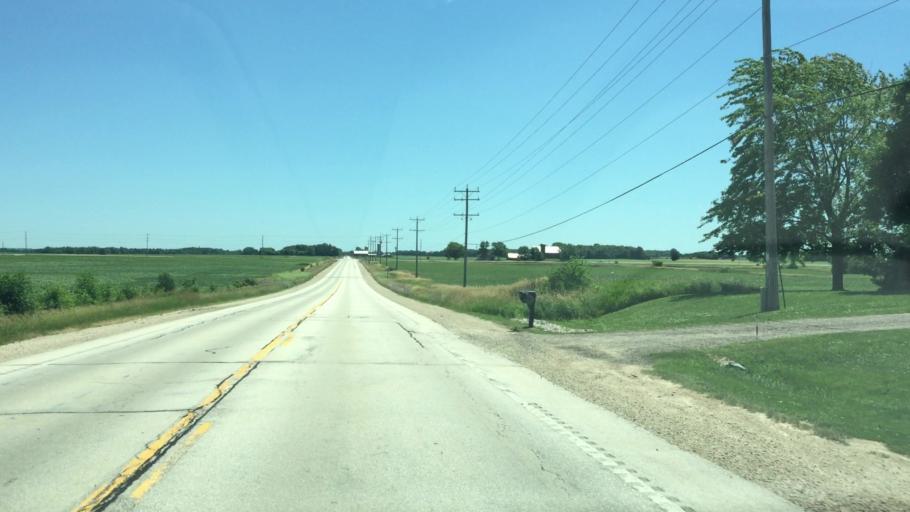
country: US
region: Wisconsin
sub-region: Calumet County
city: Hilbert
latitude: 44.1404
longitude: -88.2126
